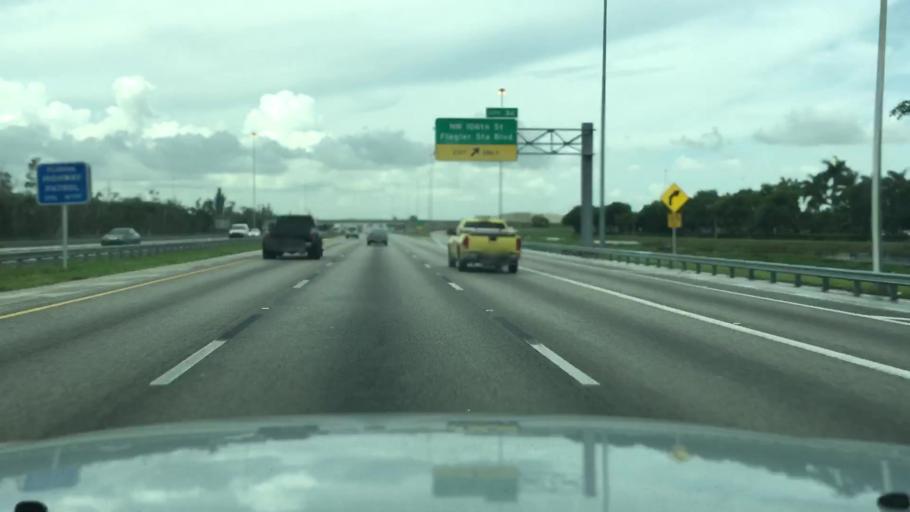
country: US
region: Florida
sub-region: Miami-Dade County
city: Doral
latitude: 25.8632
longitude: -80.3889
